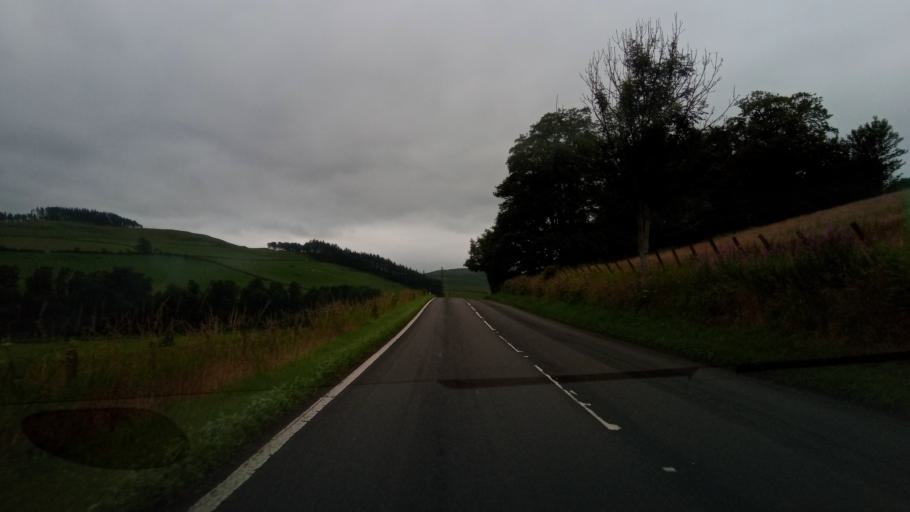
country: GB
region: Scotland
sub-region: The Scottish Borders
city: Hawick
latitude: 55.3687
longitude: -2.8802
